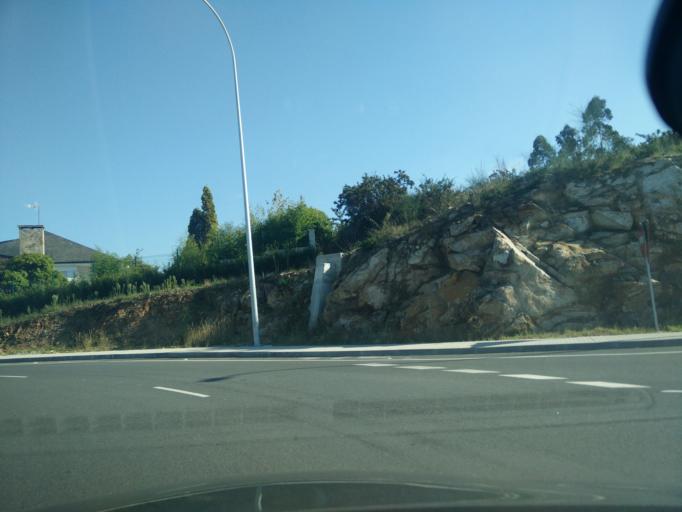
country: ES
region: Galicia
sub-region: Provincia da Coruna
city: Culleredo
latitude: 43.3223
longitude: -8.4106
